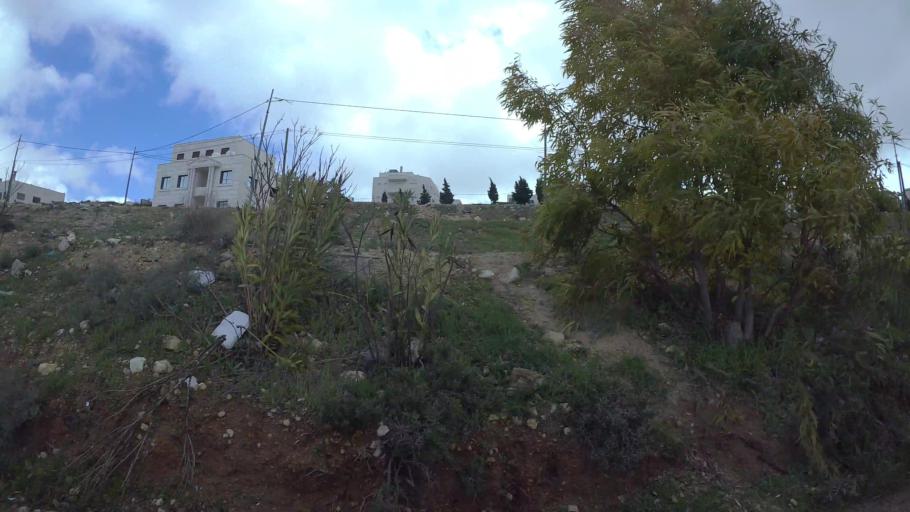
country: JO
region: Amman
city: Al Jubayhah
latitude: 32.0686
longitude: 35.8780
